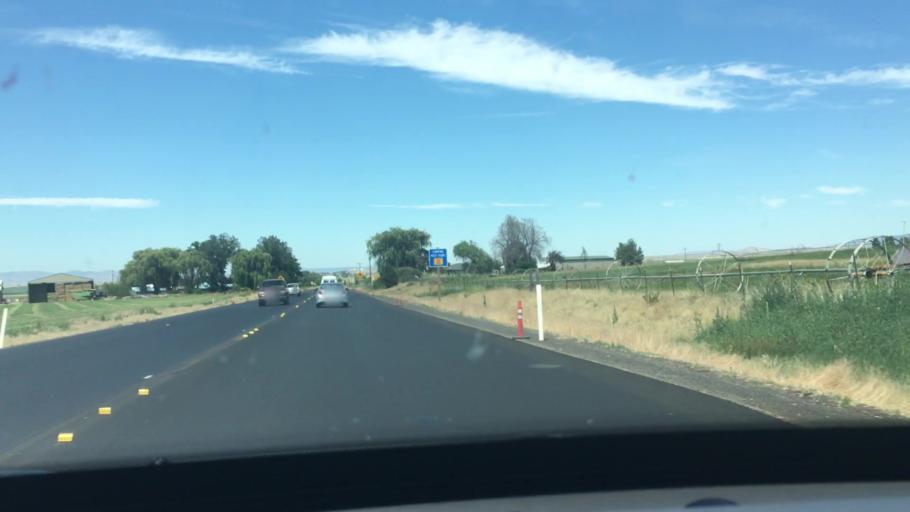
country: US
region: Oregon
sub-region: Jefferson County
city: Culver
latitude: 44.4989
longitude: -121.1911
